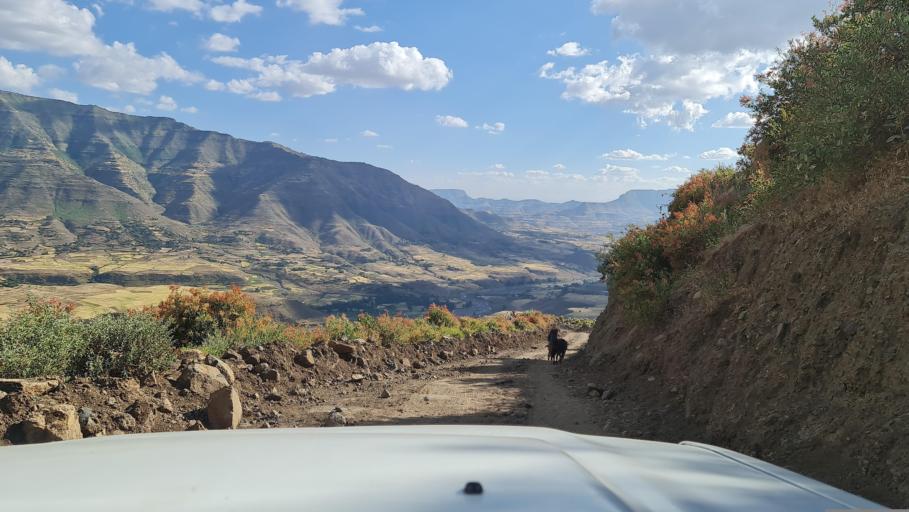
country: ET
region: Amhara
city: Debark'
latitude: 13.1226
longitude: 38.0210
